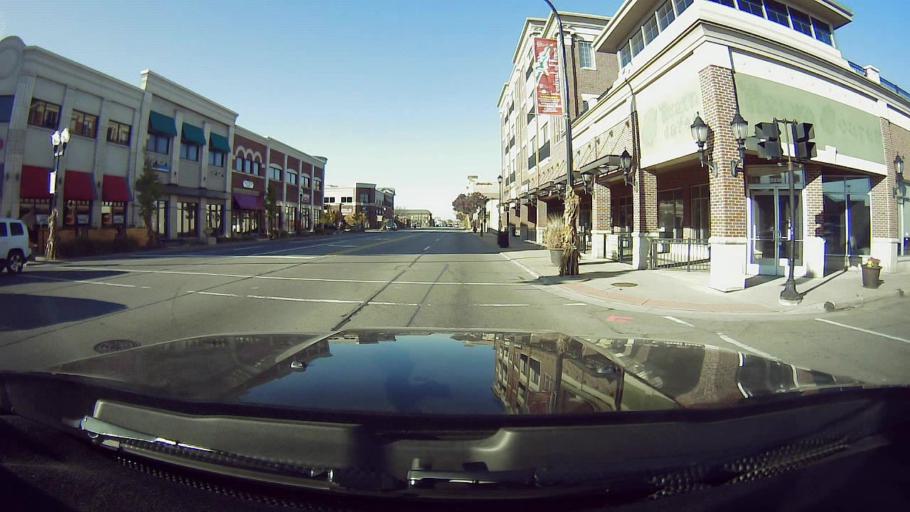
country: US
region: Michigan
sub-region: Wayne County
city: Dearborn Heights
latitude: 42.3054
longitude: -83.2478
